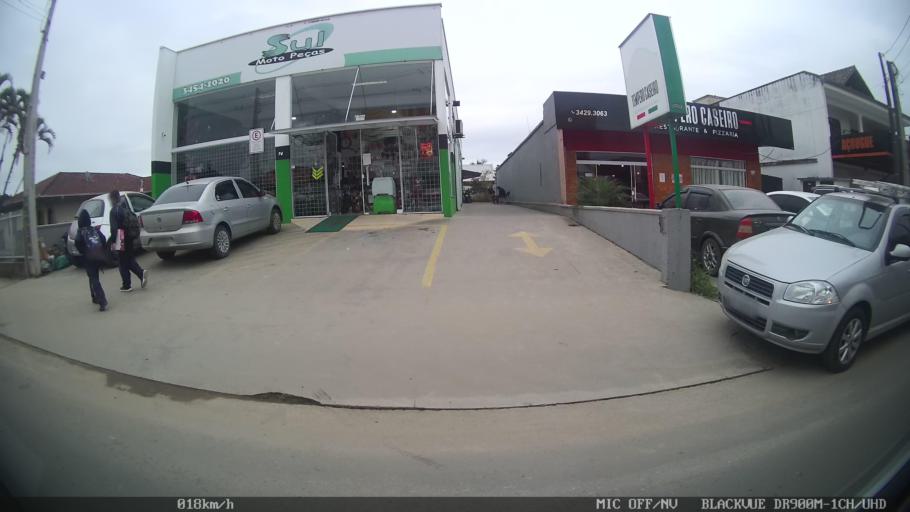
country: BR
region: Santa Catarina
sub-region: Joinville
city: Joinville
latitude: -26.3473
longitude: -48.7920
